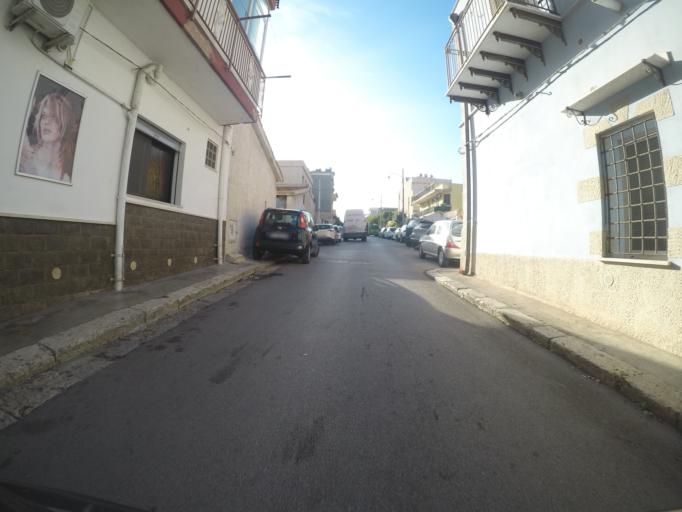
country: IT
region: Sicily
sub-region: Palermo
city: Isola delle Femmine
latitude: 38.1988
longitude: 13.2771
